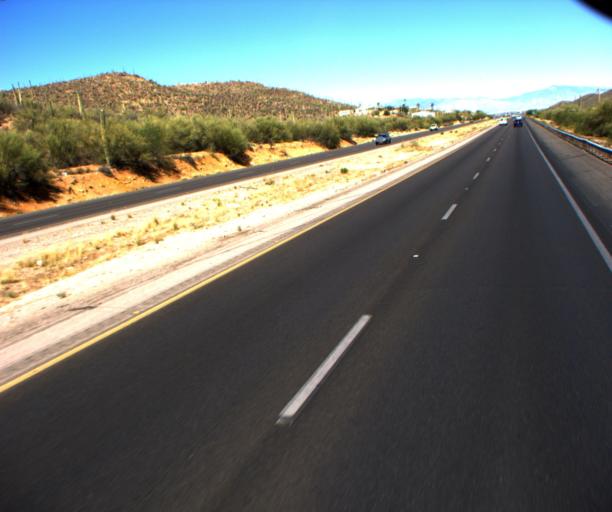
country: US
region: Arizona
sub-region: Pima County
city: Drexel Heights
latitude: 32.1769
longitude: -111.0333
